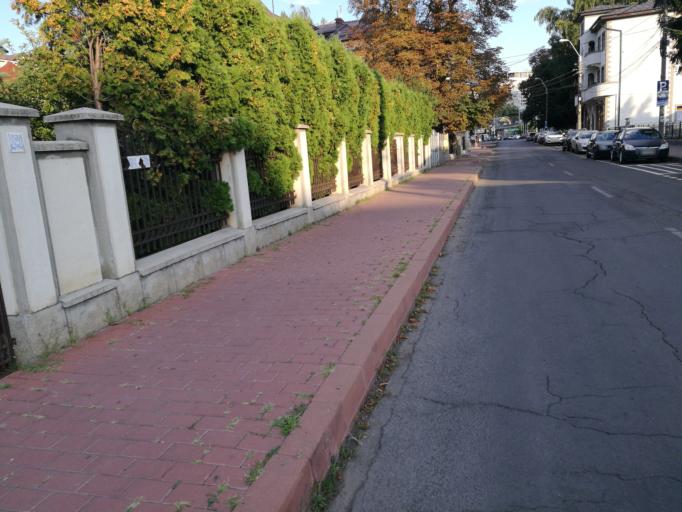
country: RO
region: Neamt
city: Piatra Neamt
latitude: 46.9329
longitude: 26.3662
